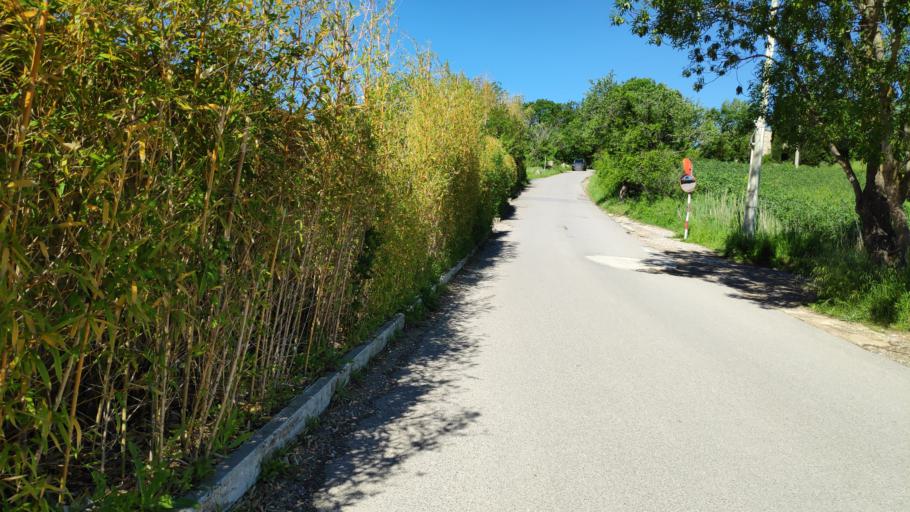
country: IT
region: Tuscany
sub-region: Provincia di Grosseto
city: Manciano
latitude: 42.6588
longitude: 11.5161
